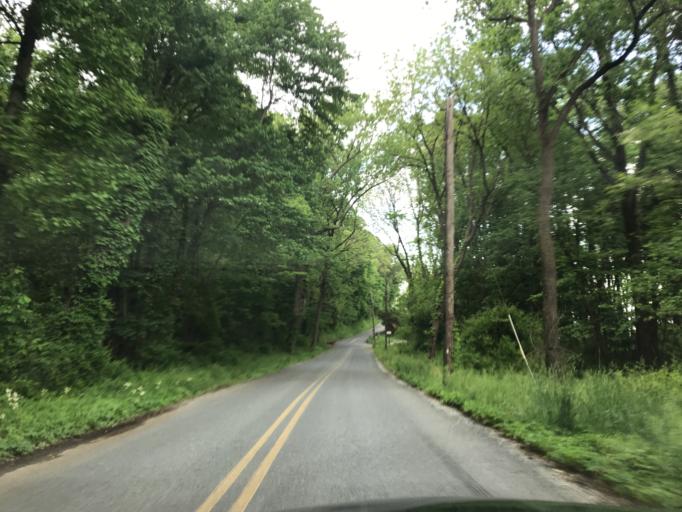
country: US
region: Pennsylvania
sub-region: York County
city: Susquehanna Trails
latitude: 39.7240
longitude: -76.3098
